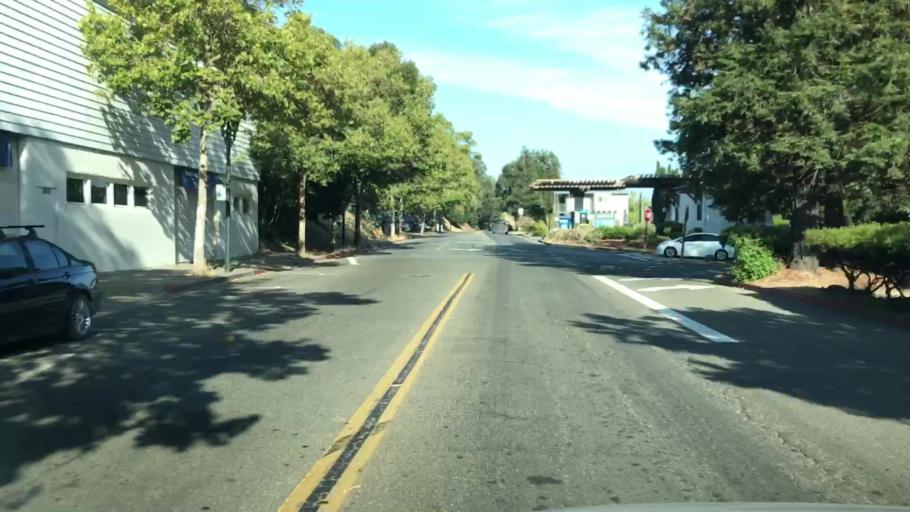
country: US
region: California
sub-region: Marin County
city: Fairfax
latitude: 37.9872
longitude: -122.5876
